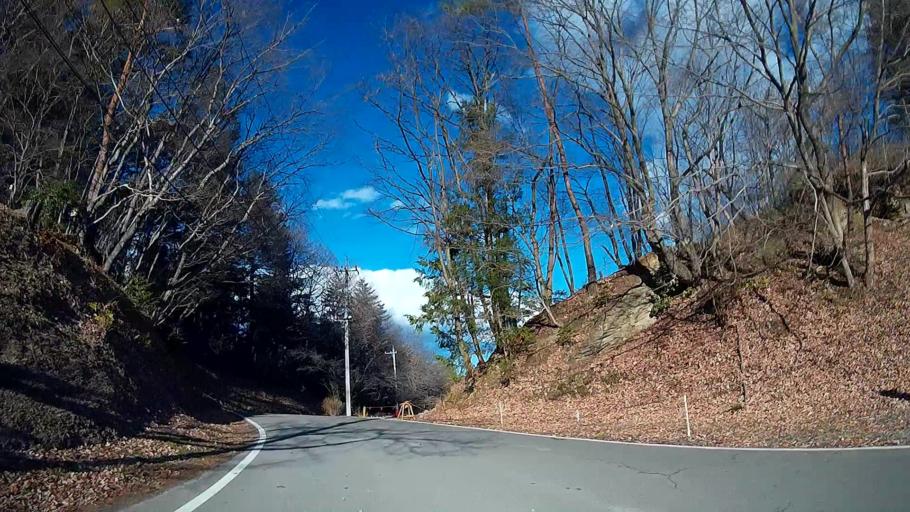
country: JP
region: Saitama
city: Yorii
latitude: 36.0907
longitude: 139.1034
